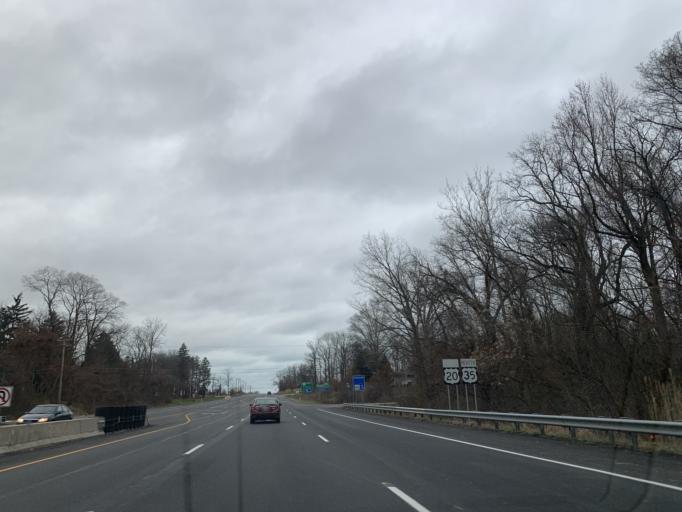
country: US
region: Indiana
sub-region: LaPorte County
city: Trail Creek
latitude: 41.6952
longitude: -86.8152
